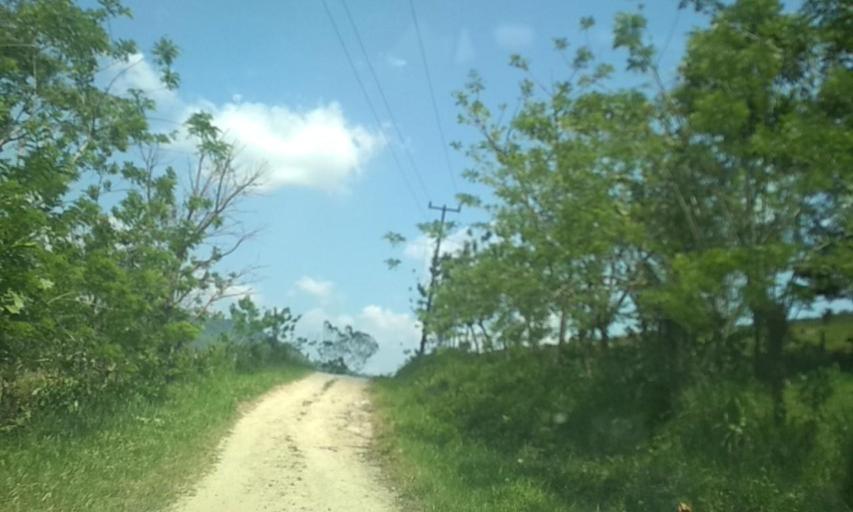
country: MX
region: Chiapas
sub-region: Tecpatan
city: Raudales Malpaso
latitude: 17.3008
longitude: -93.8206
